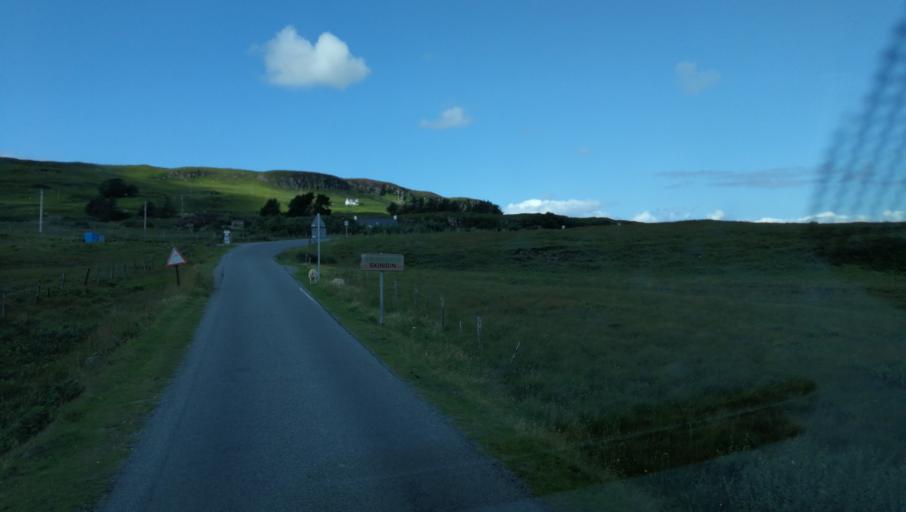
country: GB
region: Scotland
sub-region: Highland
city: Isle of Skye
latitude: 57.4312
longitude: -6.6231
